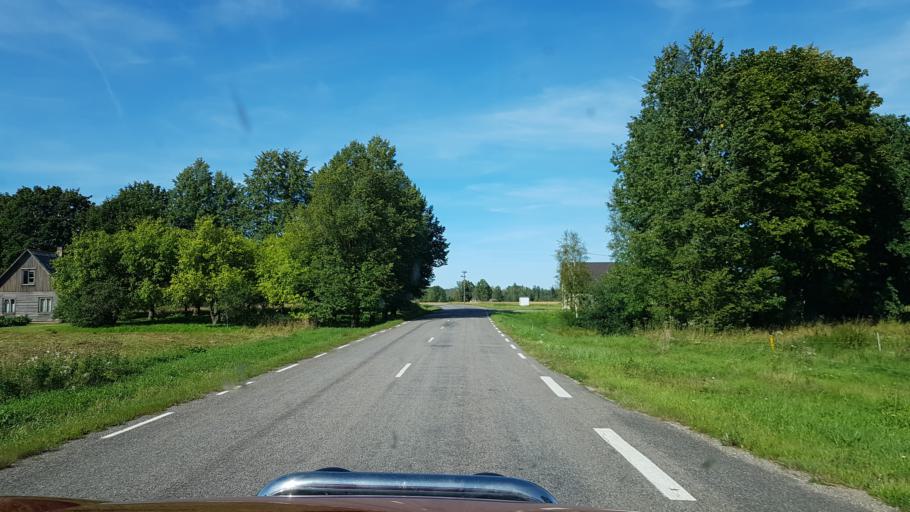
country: EE
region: Paernumaa
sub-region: Saarde vald
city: Kilingi-Nomme
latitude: 58.0435
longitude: 25.0155
